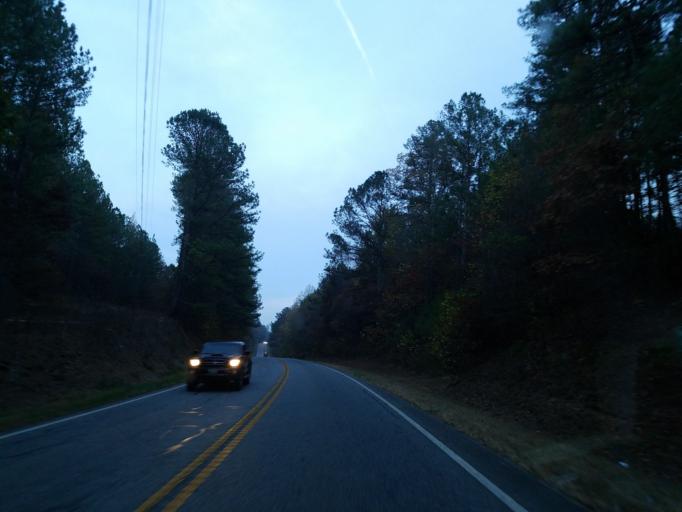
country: US
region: Georgia
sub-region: Gilmer County
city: Ellijay
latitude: 34.5621
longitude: -84.6085
